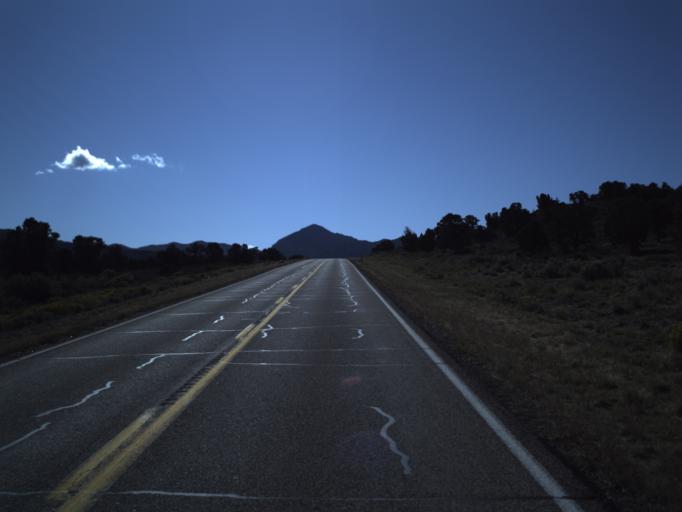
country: US
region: Utah
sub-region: Washington County
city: Enterprise
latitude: 37.6451
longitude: -113.4432
